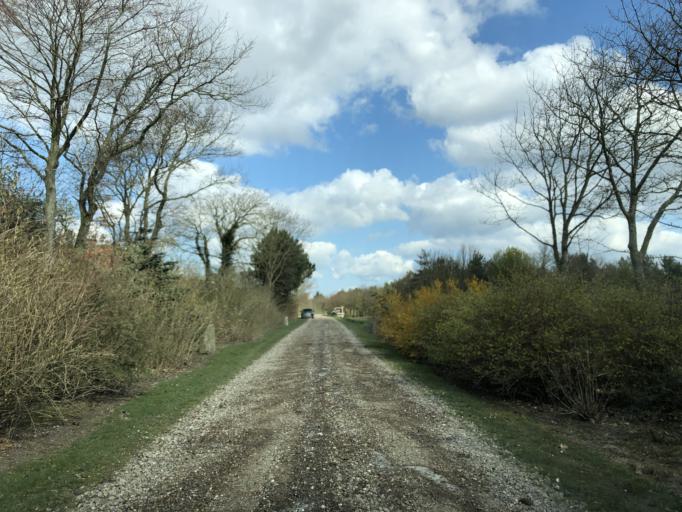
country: DK
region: Central Jutland
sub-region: Holstebro Kommune
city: Ulfborg
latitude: 56.3813
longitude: 8.2096
